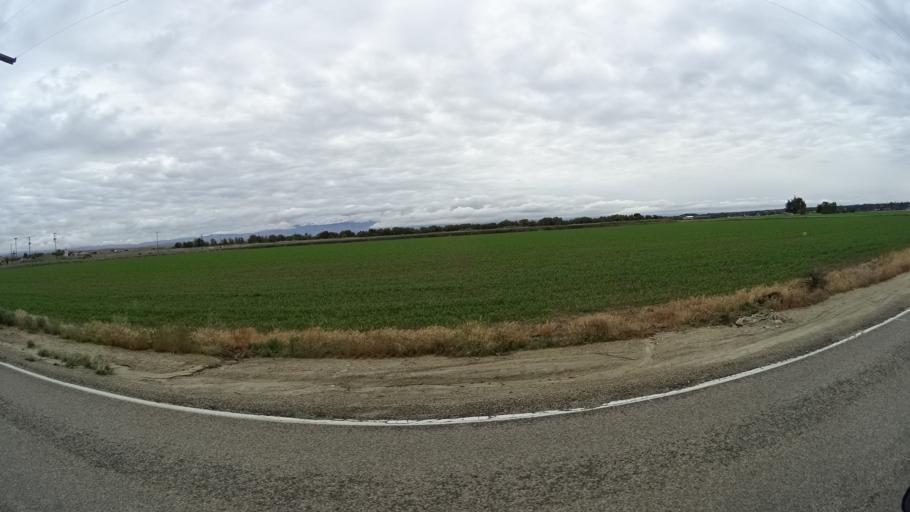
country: US
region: Idaho
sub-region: Ada County
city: Star
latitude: 43.7124
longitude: -116.4434
